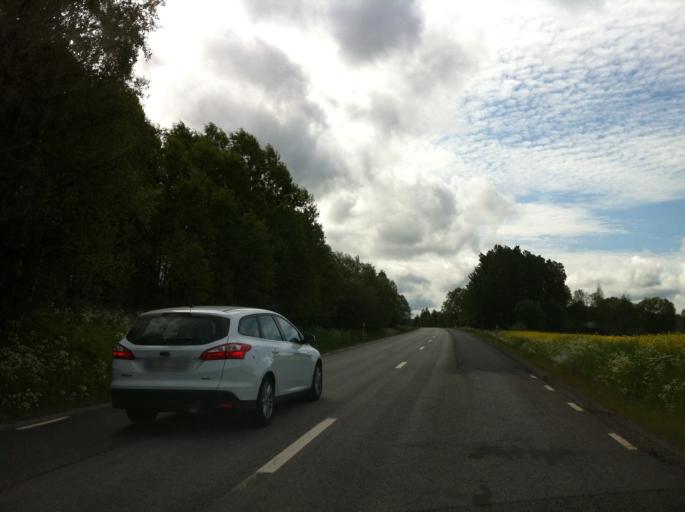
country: SE
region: Vaermland
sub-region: Sunne Kommun
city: Sunne
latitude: 59.7246
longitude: 13.1340
